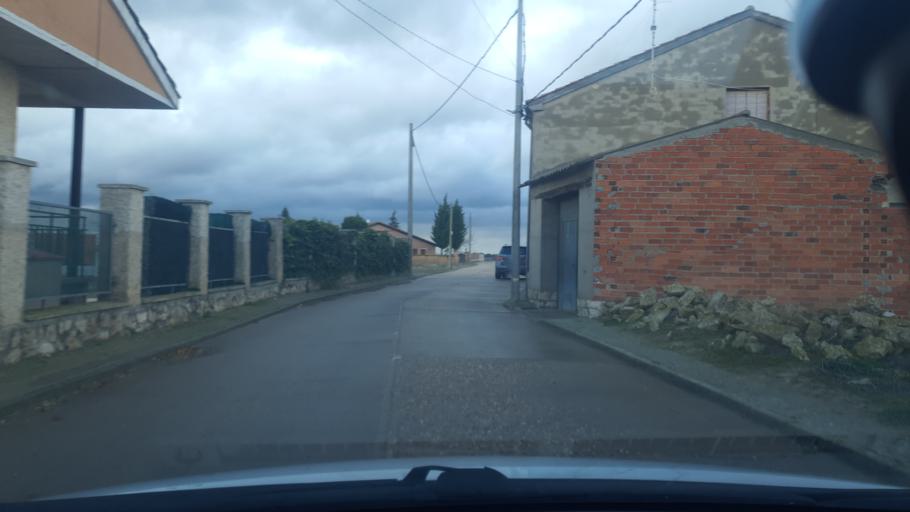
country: ES
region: Castille and Leon
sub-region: Provincia de Segovia
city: Sanchonuno
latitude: 41.2905
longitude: -4.3286
